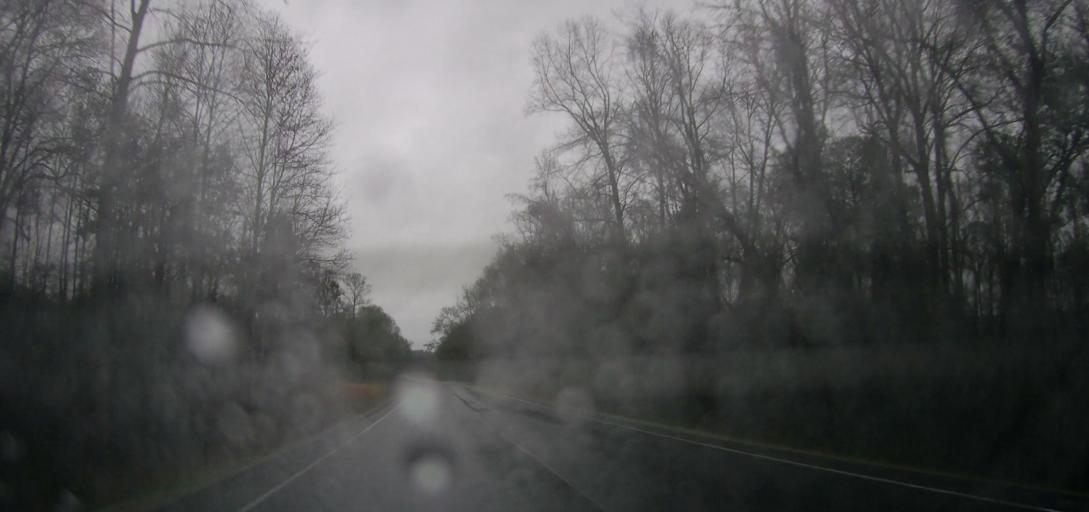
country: US
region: Alabama
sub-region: Autauga County
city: Pine Level
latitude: 32.5598
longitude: -86.6664
